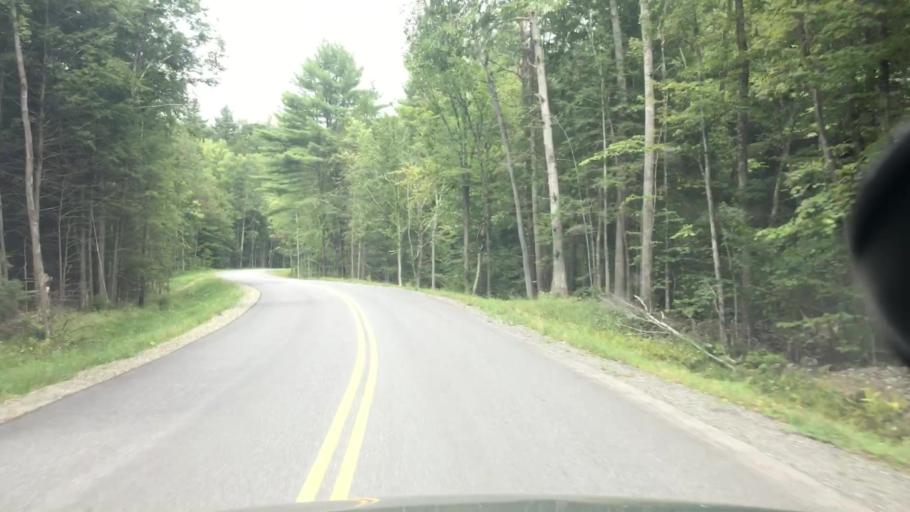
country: US
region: Massachusetts
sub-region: Franklin County
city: Colrain
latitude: 42.7623
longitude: -72.7624
